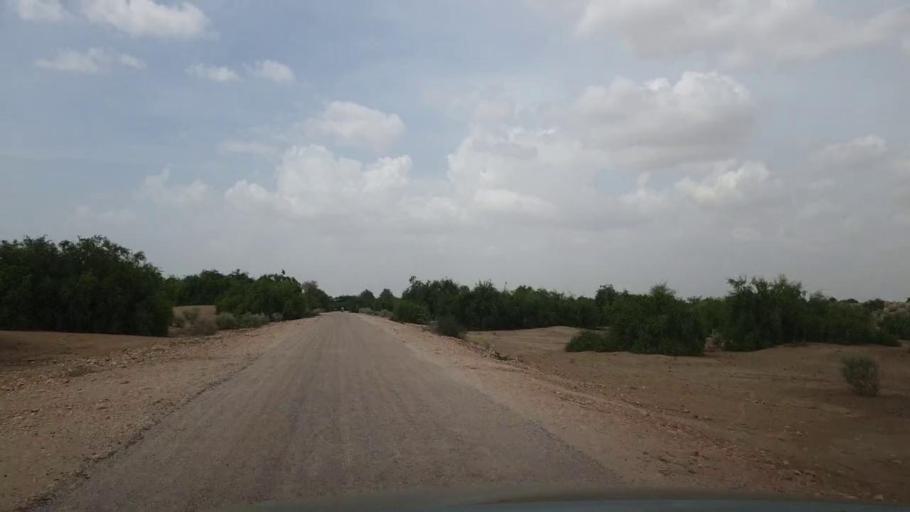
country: PK
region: Sindh
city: Kot Diji
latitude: 27.2188
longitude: 69.0839
